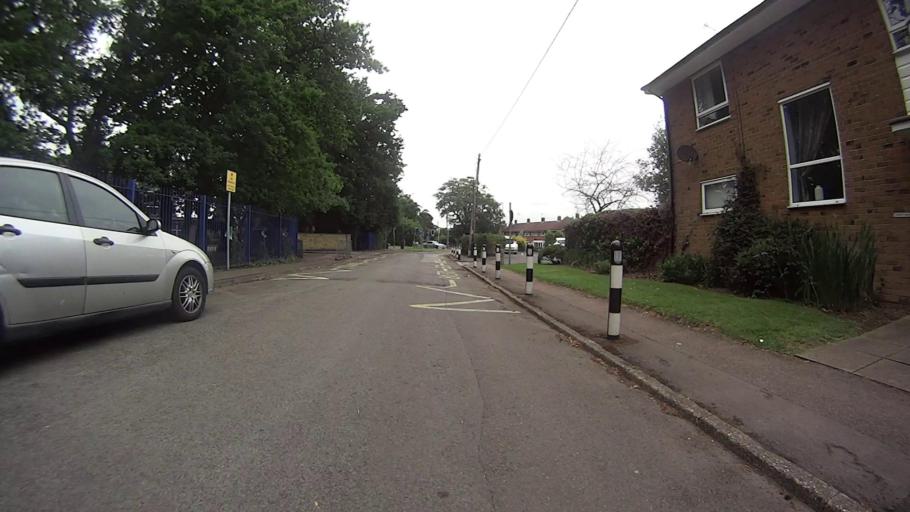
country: GB
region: England
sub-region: West Sussex
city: Langley Green
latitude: 51.1214
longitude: -0.2062
